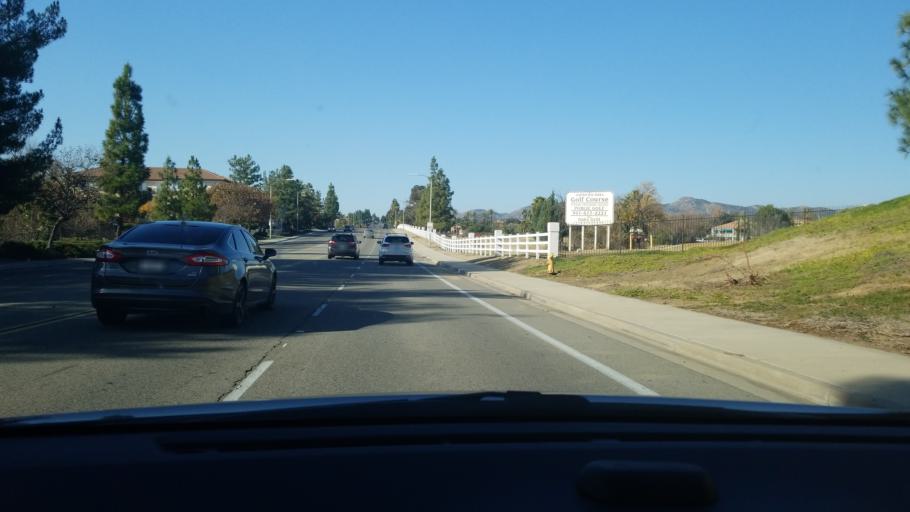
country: US
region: California
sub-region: Riverside County
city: Murrieta
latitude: 33.5731
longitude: -117.2057
